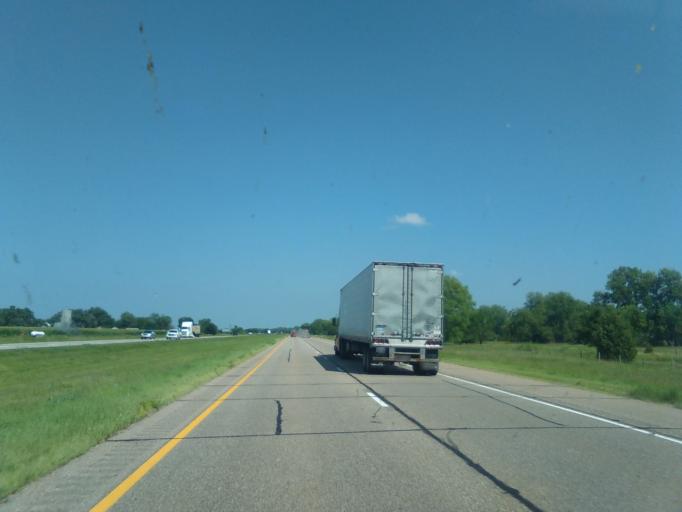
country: US
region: Nebraska
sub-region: Buffalo County
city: Kearney
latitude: 40.6737
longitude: -99.2345
